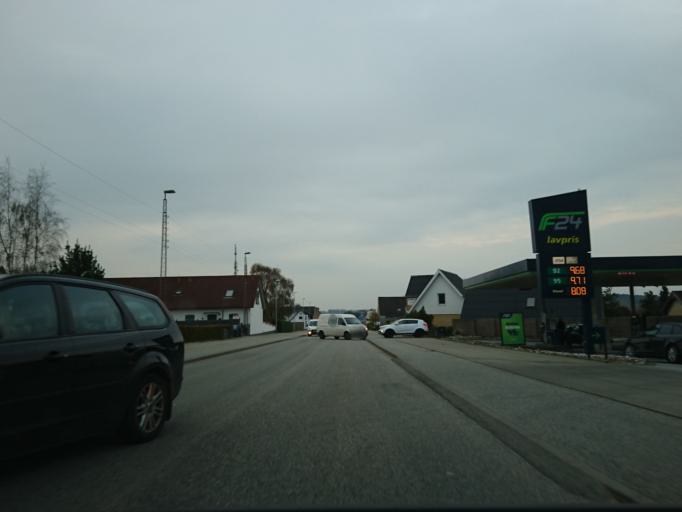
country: DK
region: North Denmark
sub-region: Alborg Kommune
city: Aalborg
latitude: 57.0104
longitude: 9.9260
